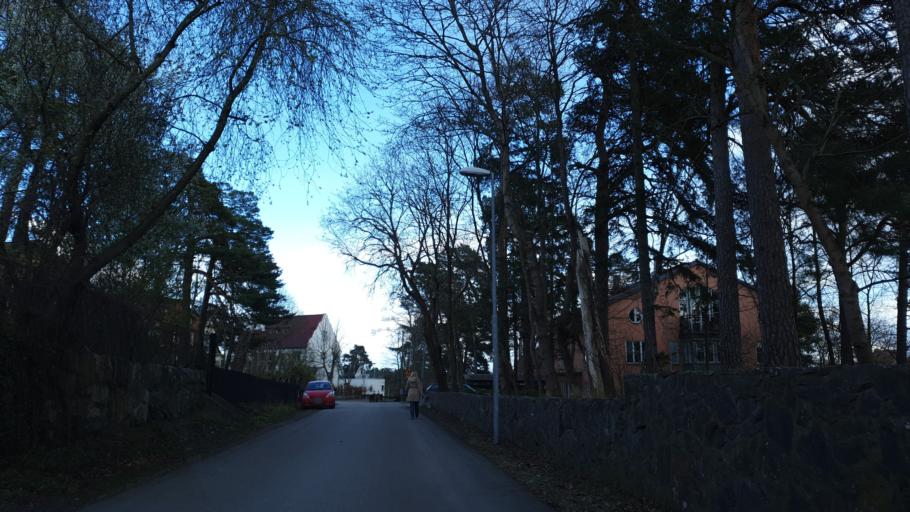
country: SE
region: Stockholm
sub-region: Lidingo
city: Lidingoe
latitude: 59.3677
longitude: 18.1354
